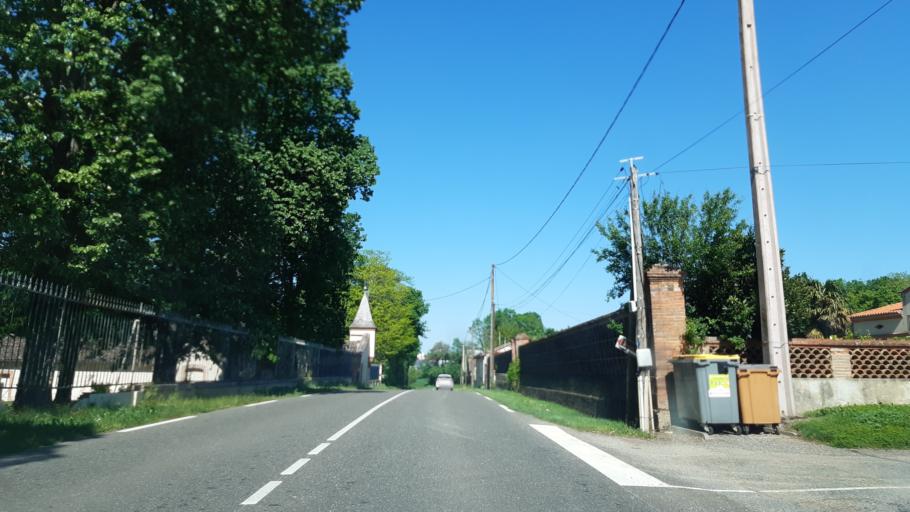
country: FR
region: Midi-Pyrenees
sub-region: Departement du Gers
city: Pujaudran
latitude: 43.5960
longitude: 1.0627
